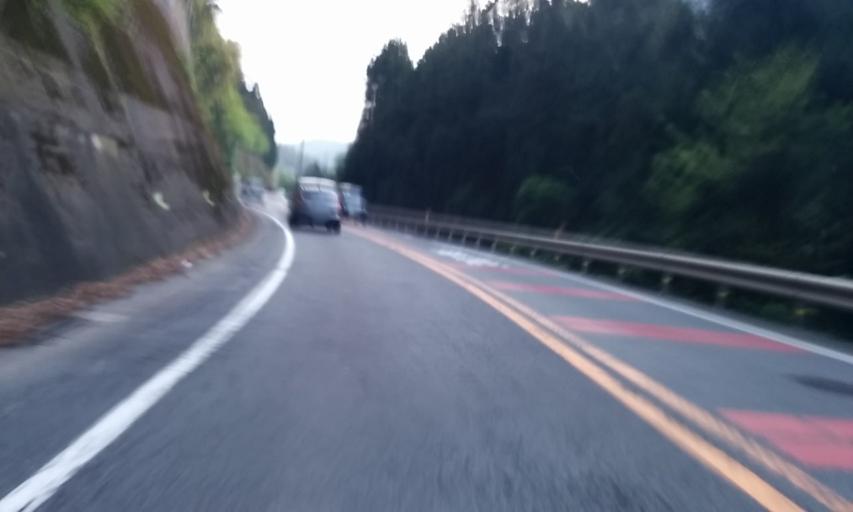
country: JP
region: Ehime
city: Saijo
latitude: 33.8288
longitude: 132.9909
